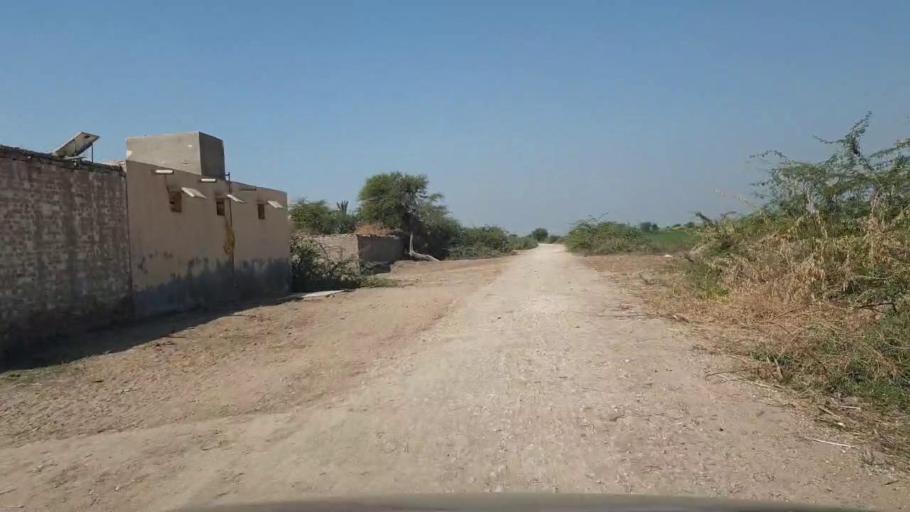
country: PK
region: Sindh
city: Samaro
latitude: 25.2351
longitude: 69.2849
